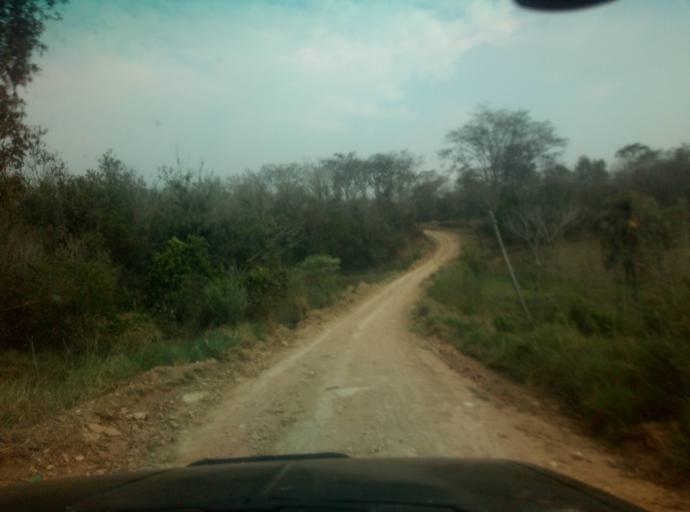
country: PY
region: Caaguazu
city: San Joaquin
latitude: -25.0922
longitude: -56.1411
